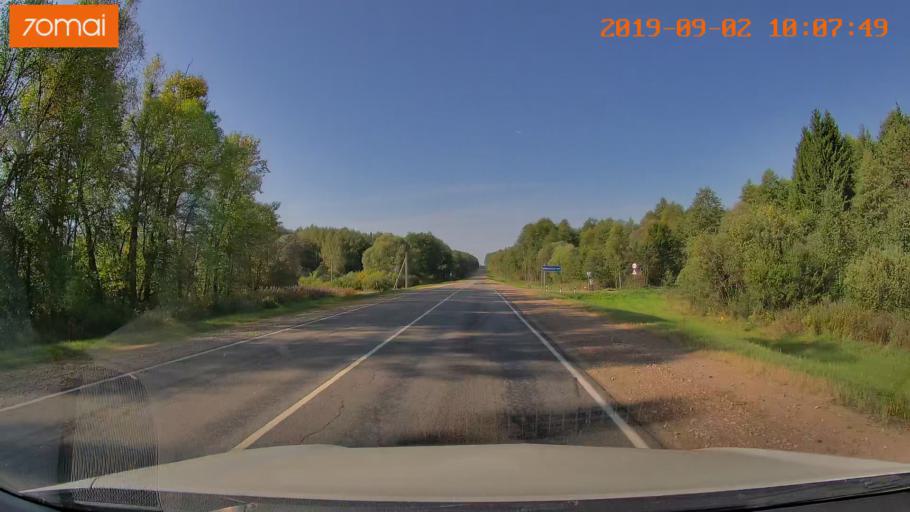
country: RU
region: Kaluga
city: Baryatino
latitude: 54.4689
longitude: 34.3756
